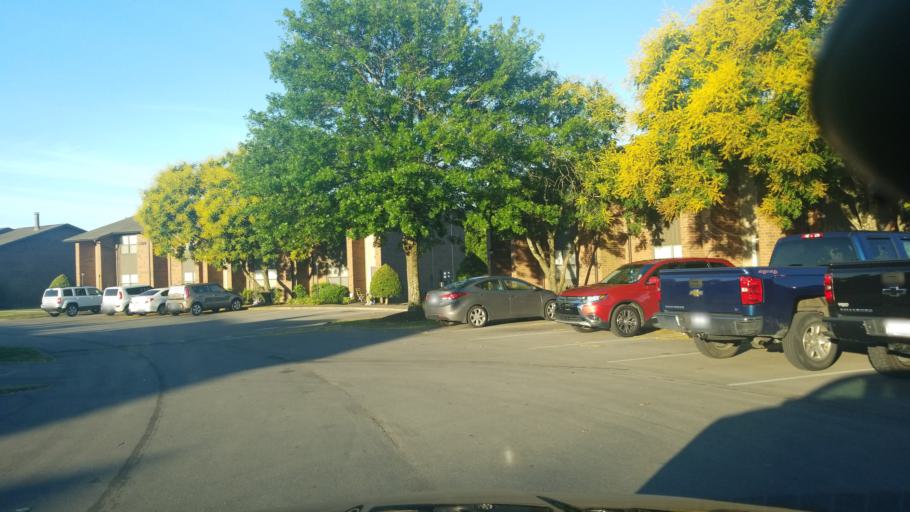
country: US
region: Tennessee
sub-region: Davidson County
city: Nashville
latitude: 36.2247
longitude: -86.7645
